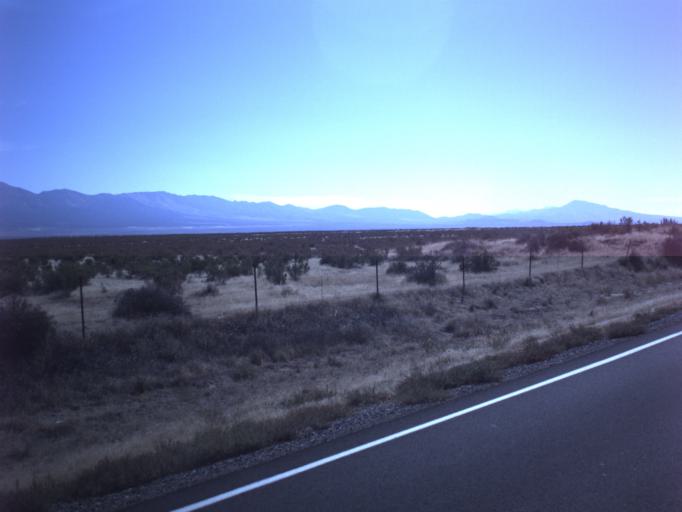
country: US
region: Utah
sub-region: Tooele County
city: Grantsville
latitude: 40.3264
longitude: -112.7441
